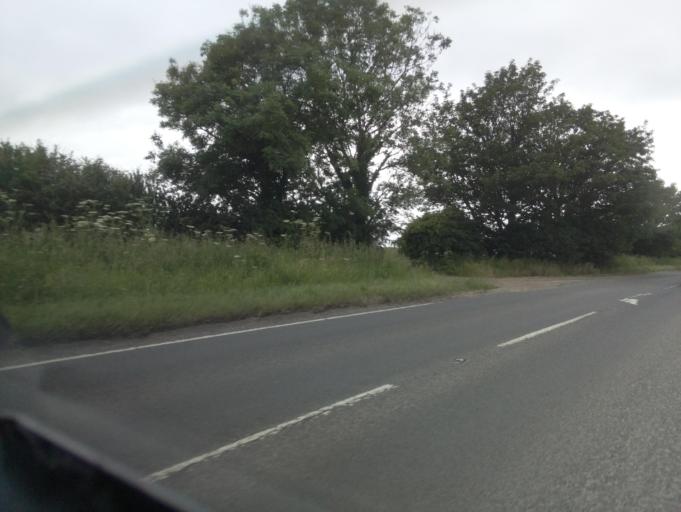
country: GB
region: England
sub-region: Staffordshire
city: Mayfield
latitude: 52.9300
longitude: -1.7636
